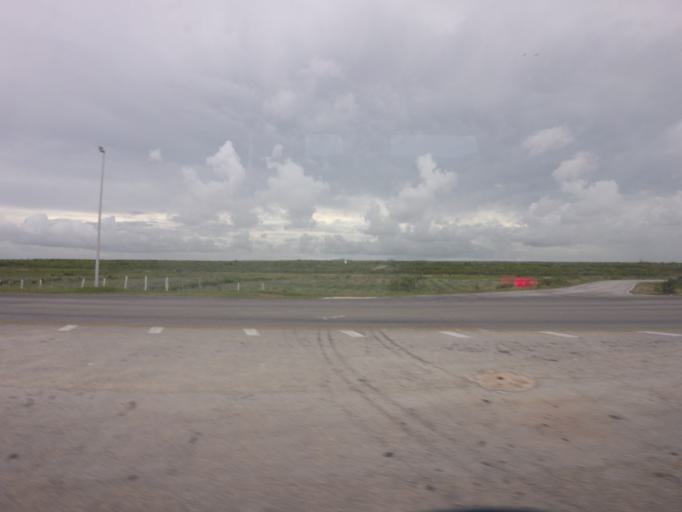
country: CU
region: Matanzas
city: Varadero
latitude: 23.1258
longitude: -81.3409
